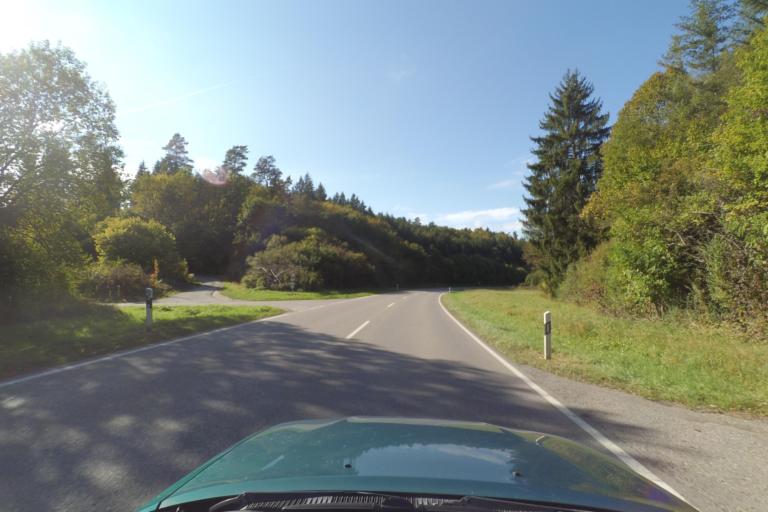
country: DE
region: Baden-Wuerttemberg
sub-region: Karlsruhe Region
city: Nagold
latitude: 48.5301
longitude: 8.7423
